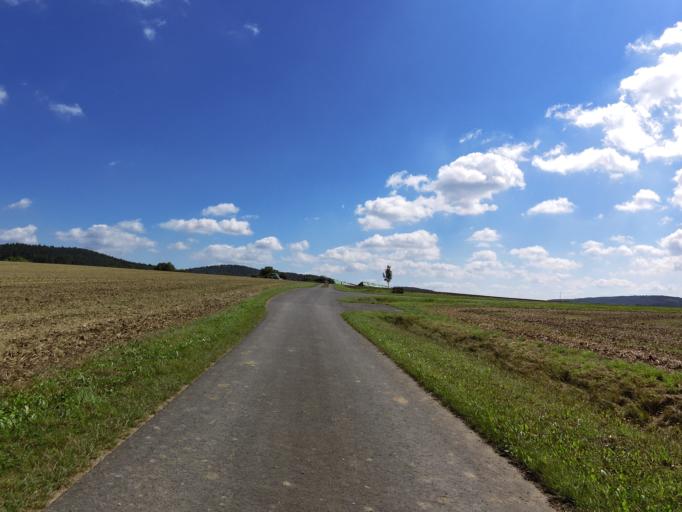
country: DE
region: Thuringia
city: Krauthausen
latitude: 51.0275
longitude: 10.2462
